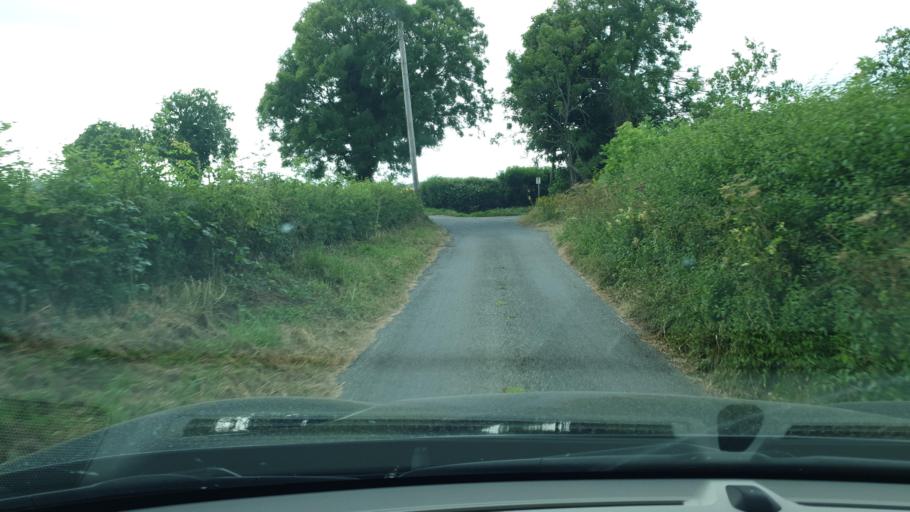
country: IE
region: Leinster
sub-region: An Mhi
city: Ratoath
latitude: 53.4731
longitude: -6.4415
